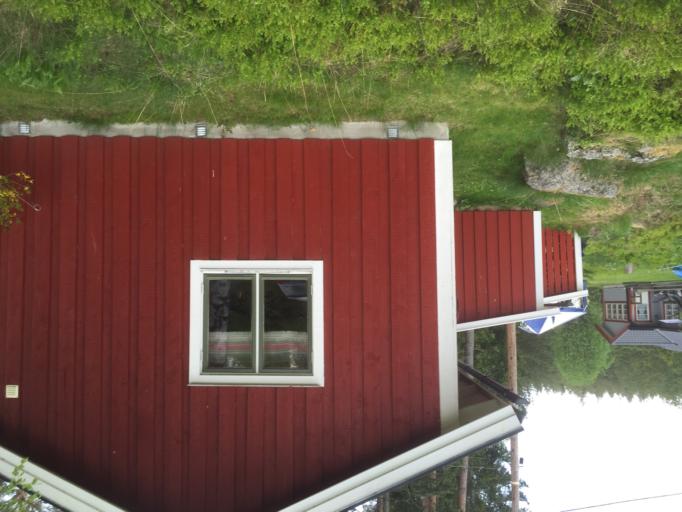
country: SE
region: Uppsala
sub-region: Alvkarleby Kommun
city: Skutskaer
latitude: 60.7899
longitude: 17.2967
